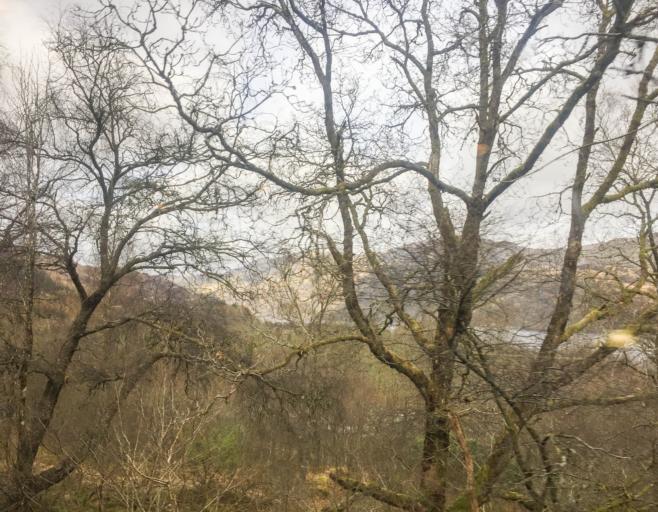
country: GB
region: Scotland
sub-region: Argyll and Bute
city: Garelochhead
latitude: 56.2436
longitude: -4.7151
